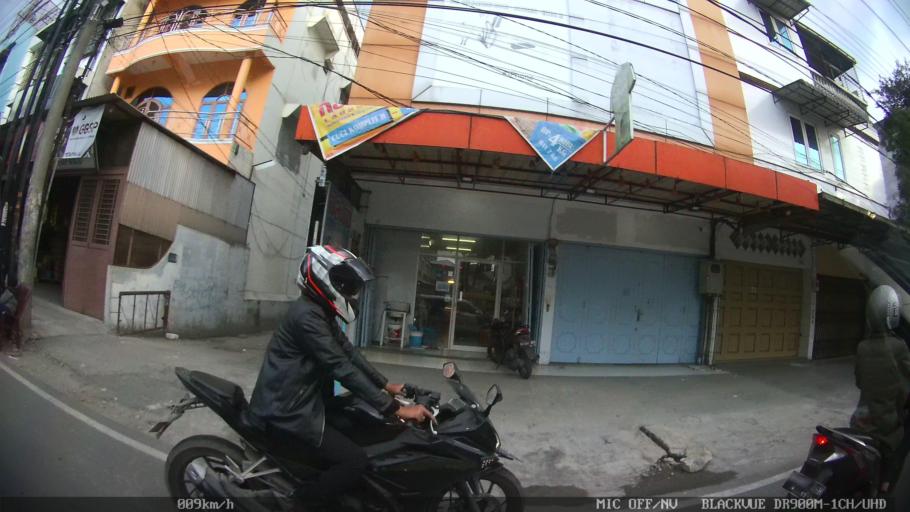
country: ID
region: North Sumatra
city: Medan
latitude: 3.5813
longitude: 98.6947
